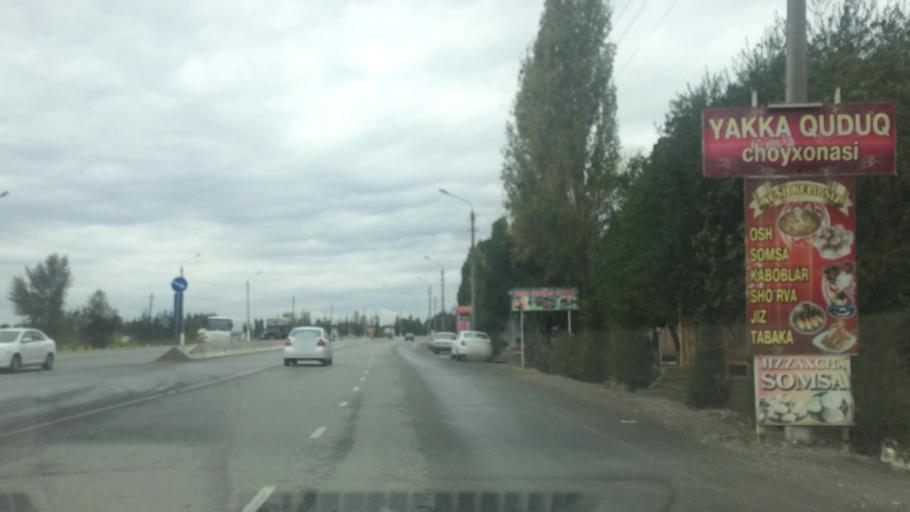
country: UZ
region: Jizzax
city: Jizzax
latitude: 39.9806
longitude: 67.5689
